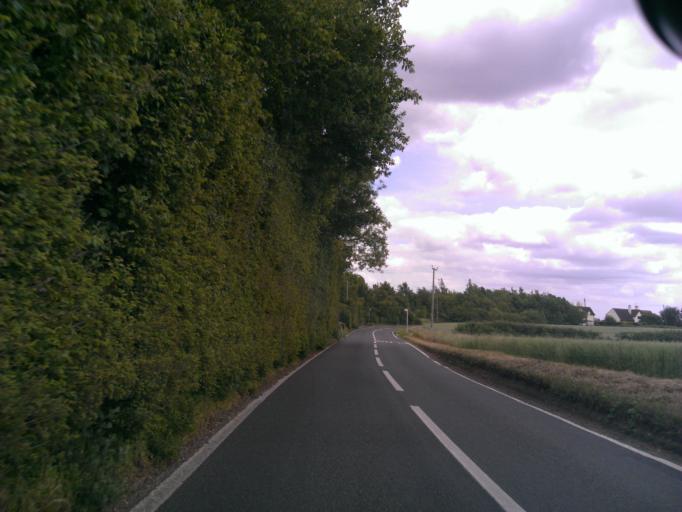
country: GB
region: England
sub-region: Essex
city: Witham
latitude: 51.8361
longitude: 0.6464
